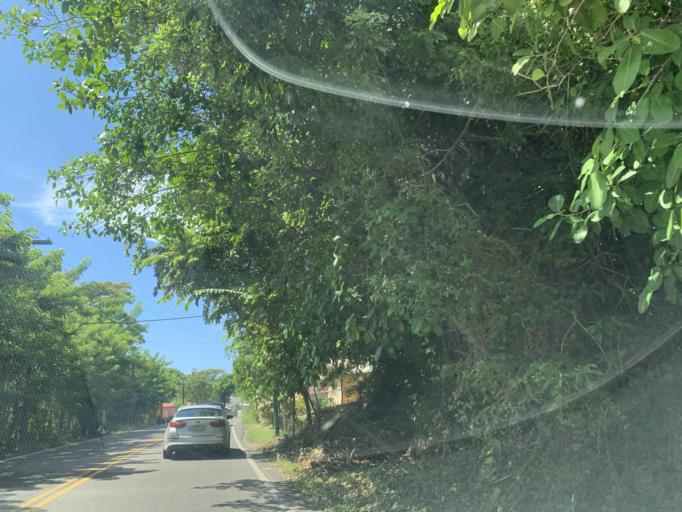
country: DO
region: Maria Trinidad Sanchez
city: Cabrera
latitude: 19.6516
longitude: -69.9326
